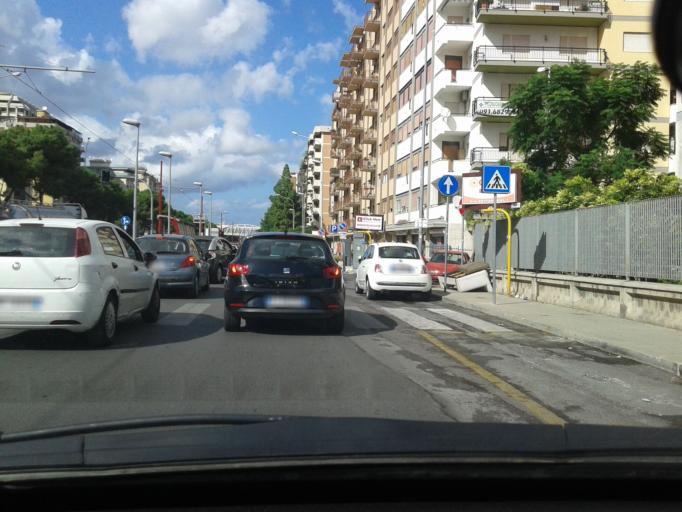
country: IT
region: Sicily
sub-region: Palermo
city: Palermo
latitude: 38.1226
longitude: 13.3293
